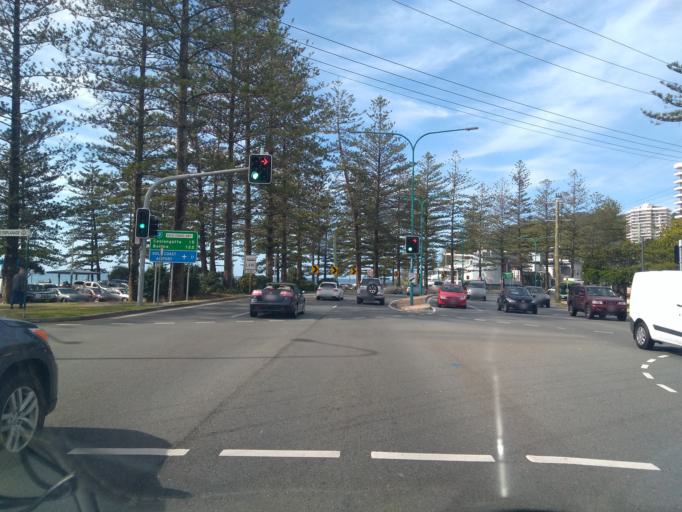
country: AU
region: Queensland
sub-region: Gold Coast
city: Burleigh Waters
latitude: -28.0885
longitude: 153.4518
